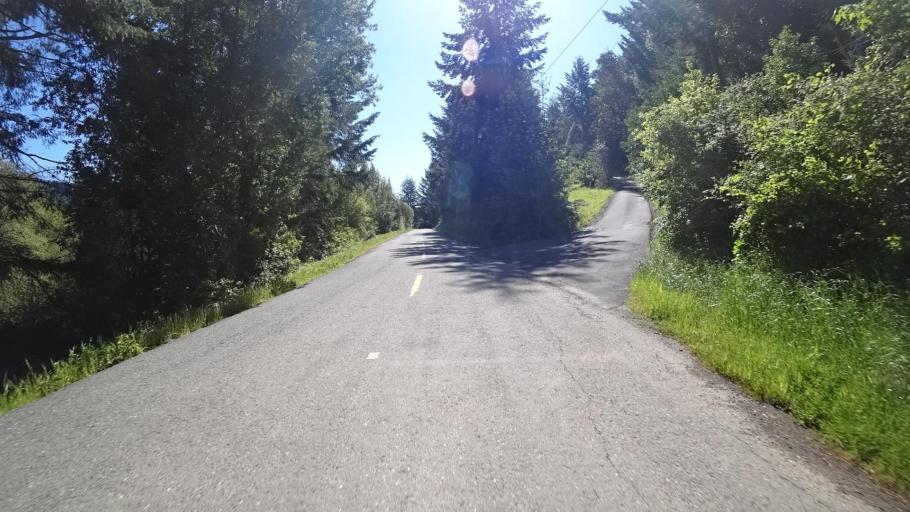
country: US
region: California
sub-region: Humboldt County
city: Rio Dell
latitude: 40.2496
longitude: -124.1781
